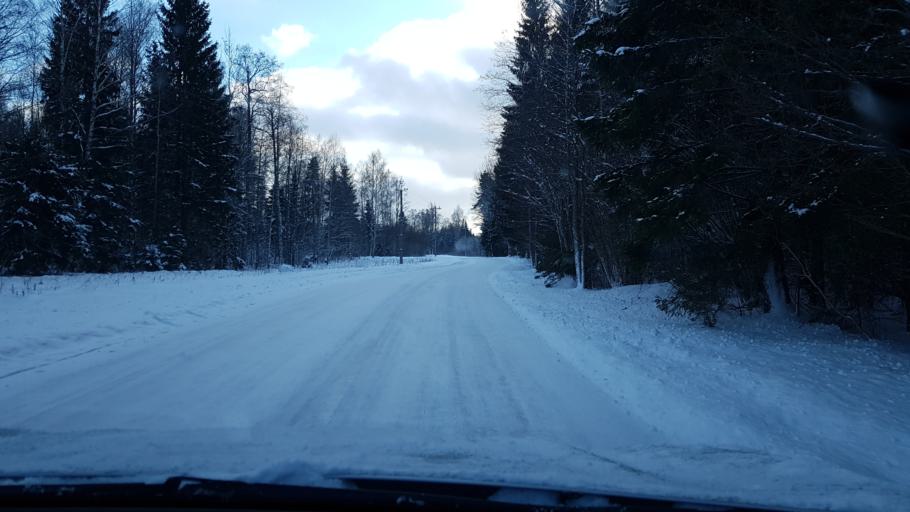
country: EE
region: Harju
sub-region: Nissi vald
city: Turba
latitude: 59.1559
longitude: 24.1444
